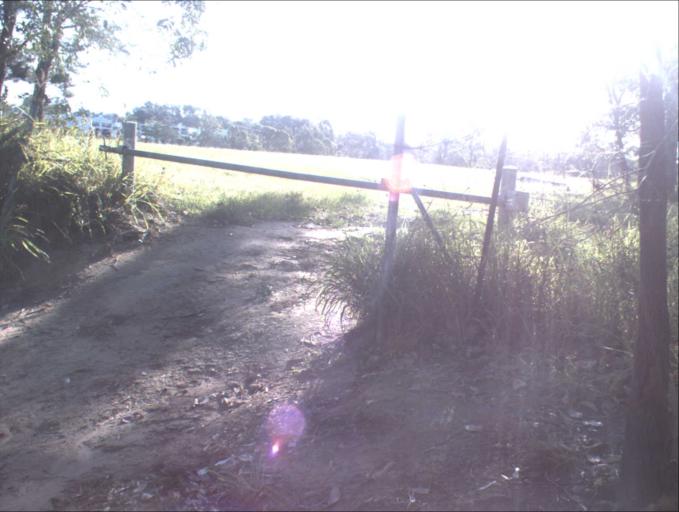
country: AU
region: Queensland
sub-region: Logan
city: Woodridge
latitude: -27.6174
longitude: 153.1059
